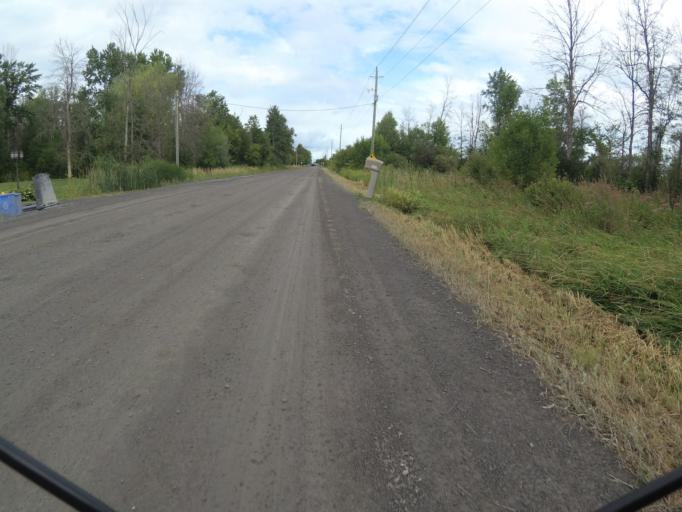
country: CA
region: Ontario
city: Clarence-Rockland
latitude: 45.4728
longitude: -75.3047
